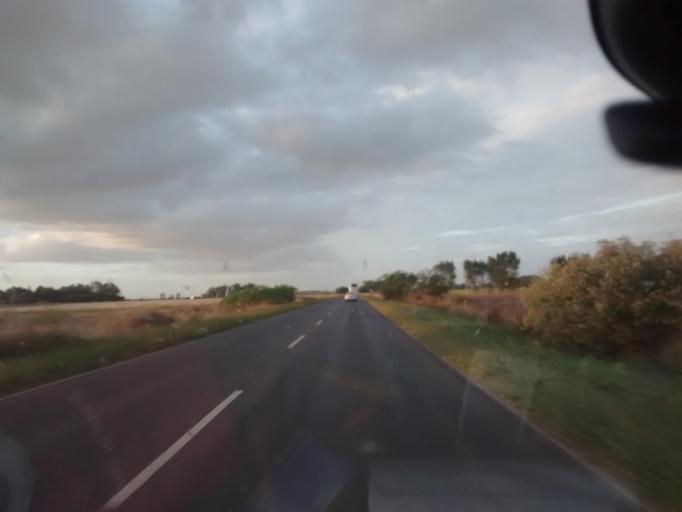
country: AR
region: Buenos Aires
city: Ranchos
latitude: -35.4987
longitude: -58.3495
